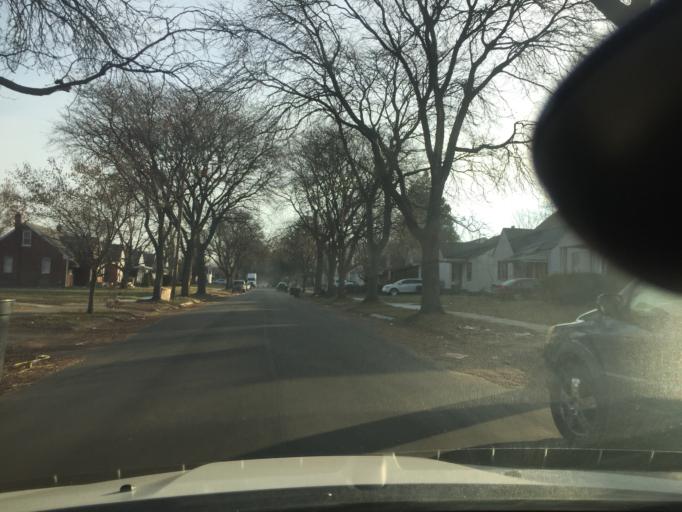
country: US
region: Michigan
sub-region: Macomb County
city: Eastpointe
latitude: 42.4436
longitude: -82.9651
